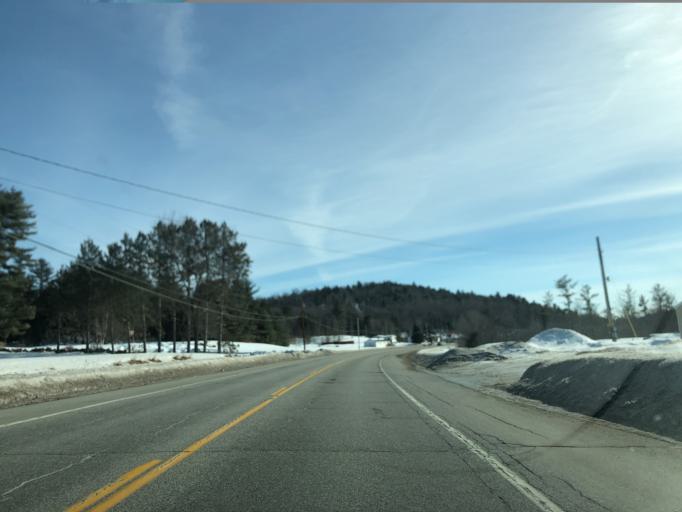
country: US
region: Maine
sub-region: Oxford County
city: West Paris
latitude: 44.3241
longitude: -70.5475
